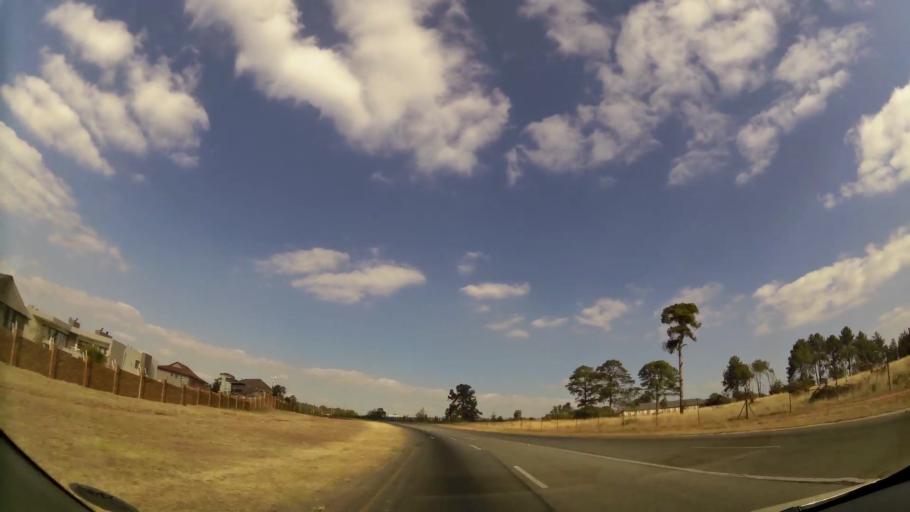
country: ZA
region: Gauteng
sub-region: West Rand District Municipality
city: Krugersdorp
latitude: -26.0558
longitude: 27.7544
